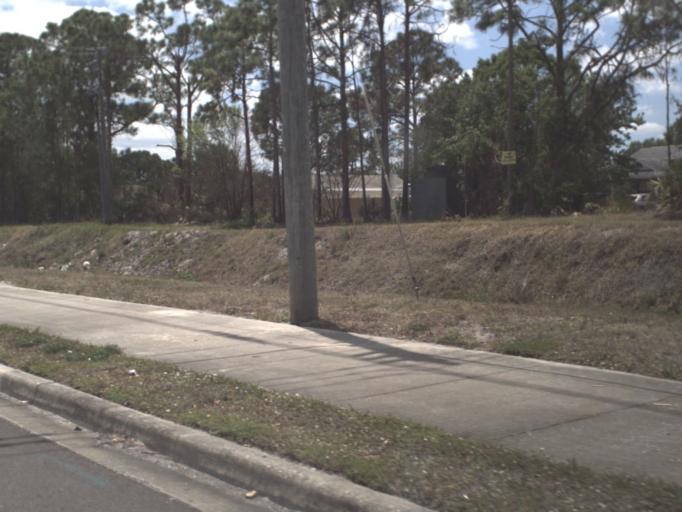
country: US
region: Florida
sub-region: Brevard County
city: Palm Bay
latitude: 28.0026
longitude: -80.6220
